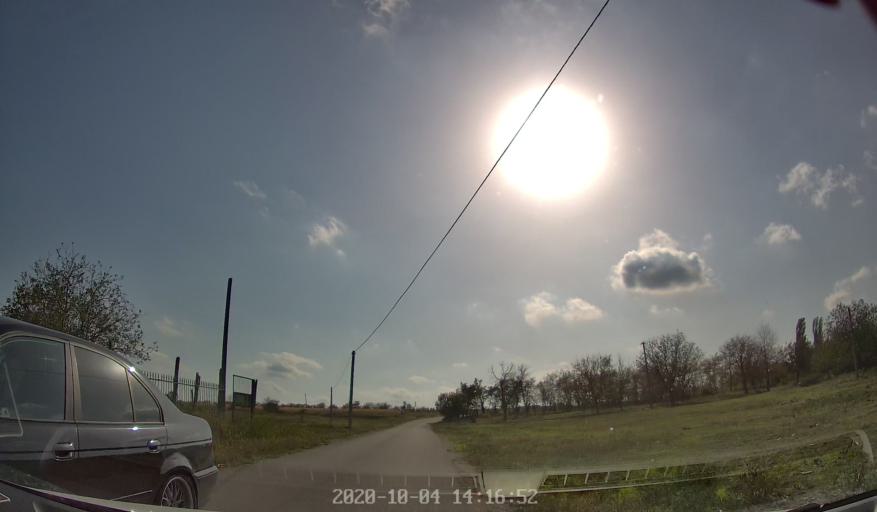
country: MD
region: Rezina
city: Saharna
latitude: 47.6027
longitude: 28.9842
